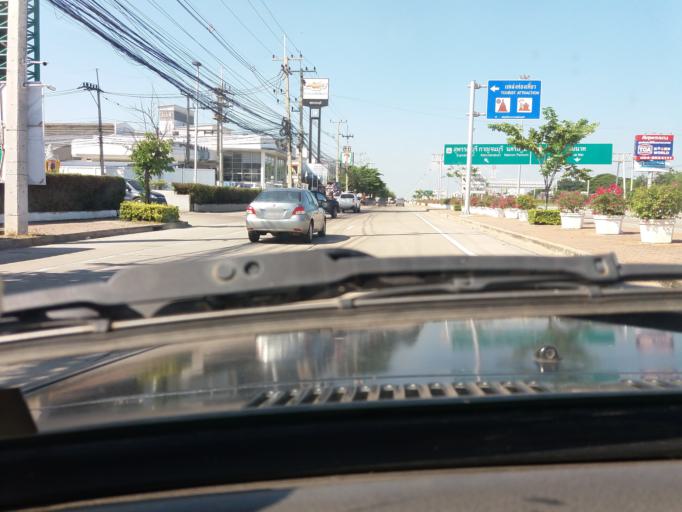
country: TH
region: Suphan Buri
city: Suphan Buri
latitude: 14.4697
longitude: 100.1312
